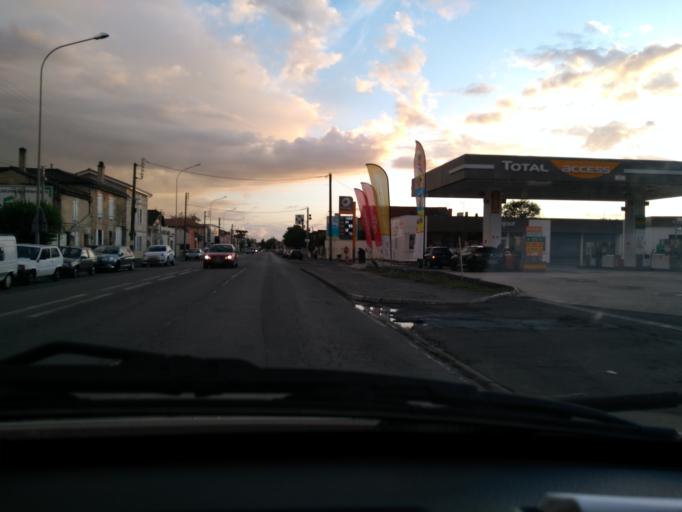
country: FR
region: Poitou-Charentes
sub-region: Departement de la Charente
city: Angouleme
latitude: 45.6428
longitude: 0.1356
